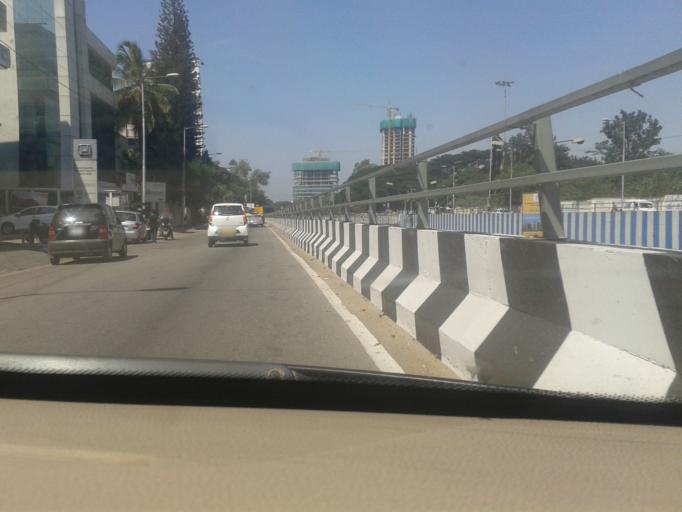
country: IN
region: Karnataka
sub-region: Bangalore Urban
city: Bangalore
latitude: 13.0130
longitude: 77.5838
